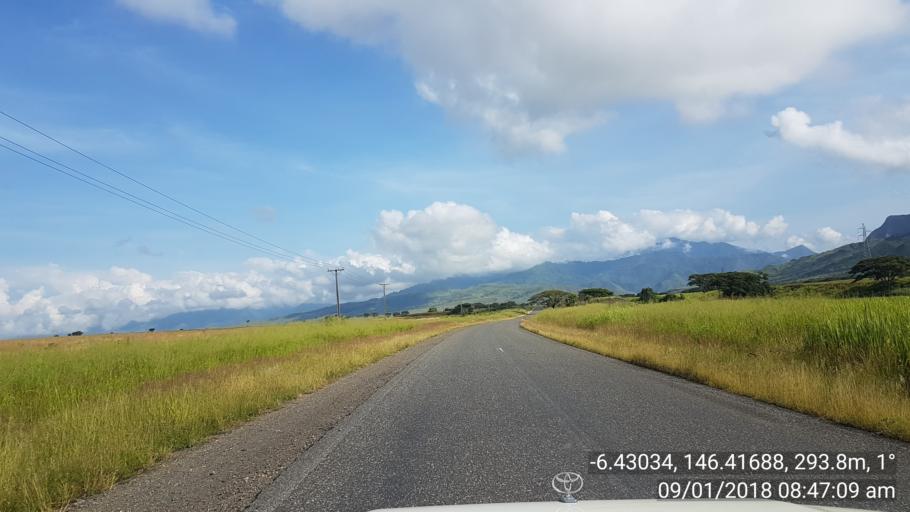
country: PG
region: Eastern Highlands
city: Kainantu
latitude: -6.4305
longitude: 146.4169
